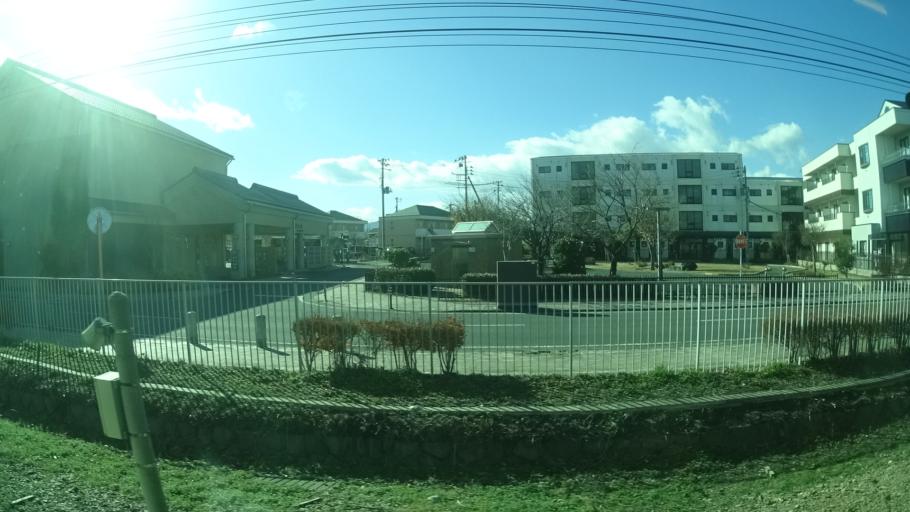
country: JP
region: Fukushima
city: Namie
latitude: 37.6391
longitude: 140.9699
